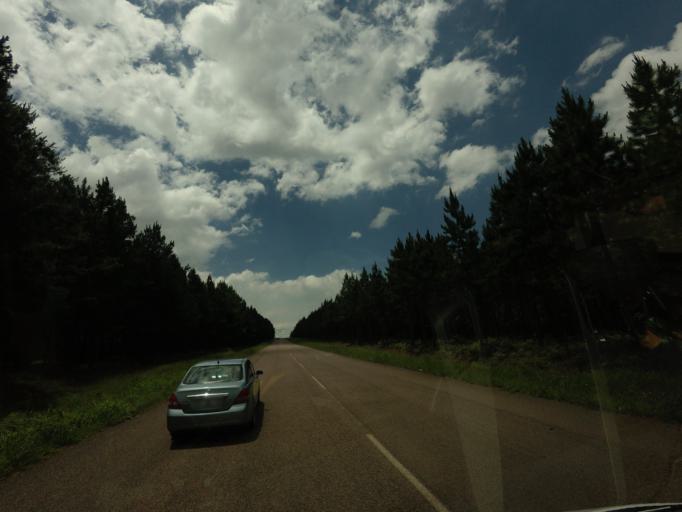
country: ZA
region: Mpumalanga
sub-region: Ehlanzeni District
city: Graksop
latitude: -25.0293
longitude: 30.8211
